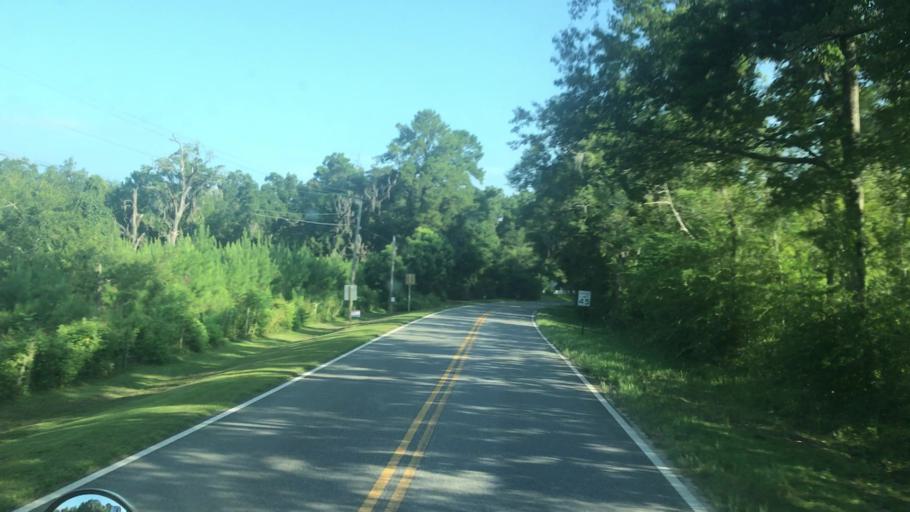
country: US
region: Florida
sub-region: Gadsden County
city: Quincy
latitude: 30.6072
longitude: -84.5731
